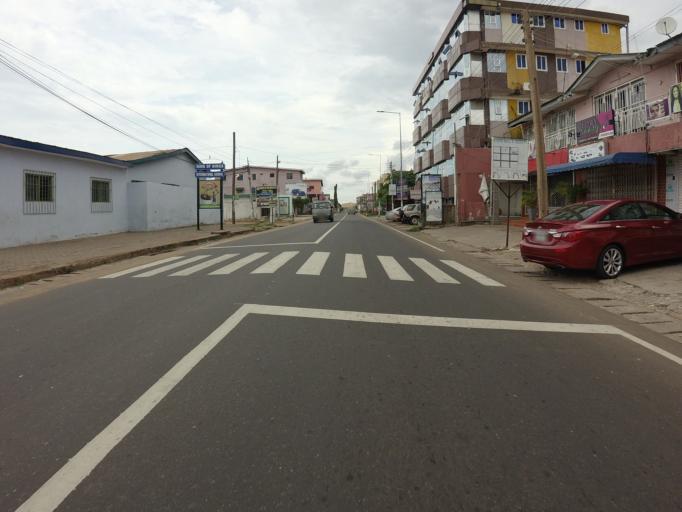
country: GH
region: Greater Accra
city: Dome
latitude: 5.6117
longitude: -0.2033
